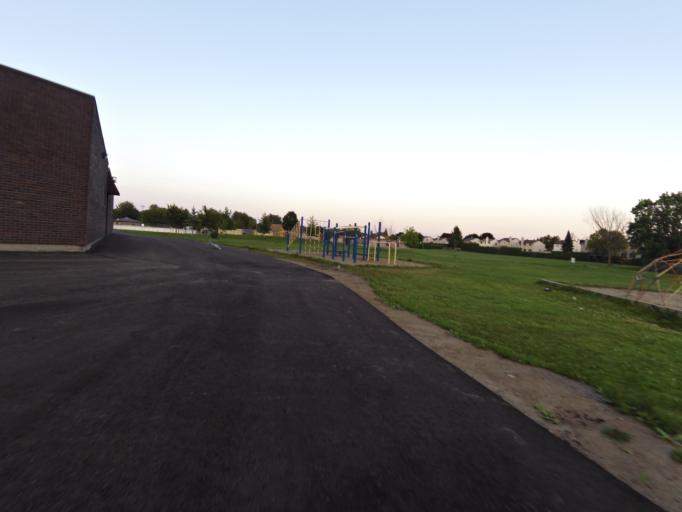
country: CA
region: Quebec
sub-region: Outaouais
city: Gatineau
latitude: 45.4671
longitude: -75.5011
